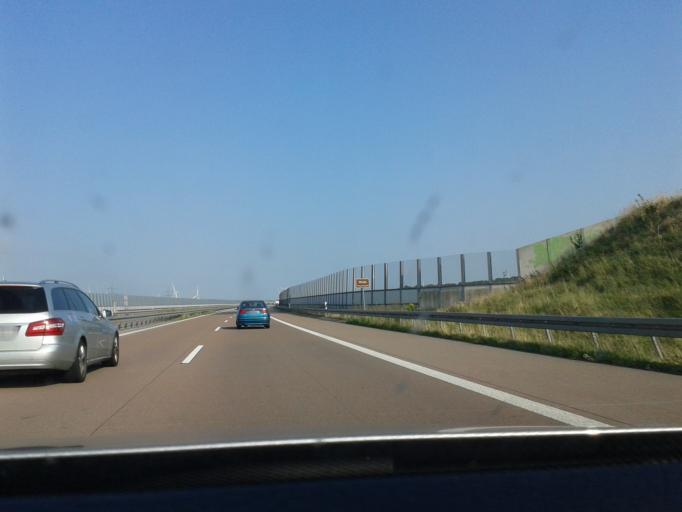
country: DE
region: Saxony-Anhalt
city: Obhausen
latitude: 51.4174
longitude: 11.6598
